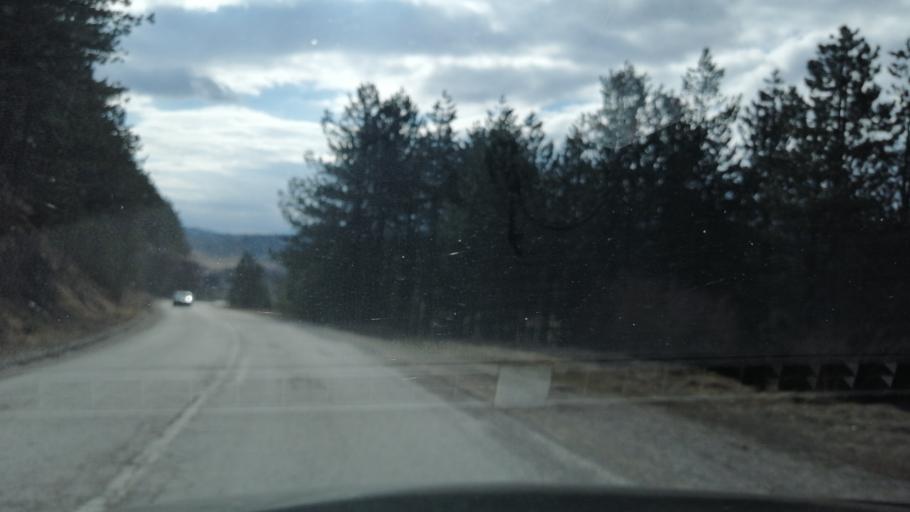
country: RS
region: Central Serbia
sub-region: Zlatiborski Okrug
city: Bajina Basta
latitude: 43.8622
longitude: 19.5776
